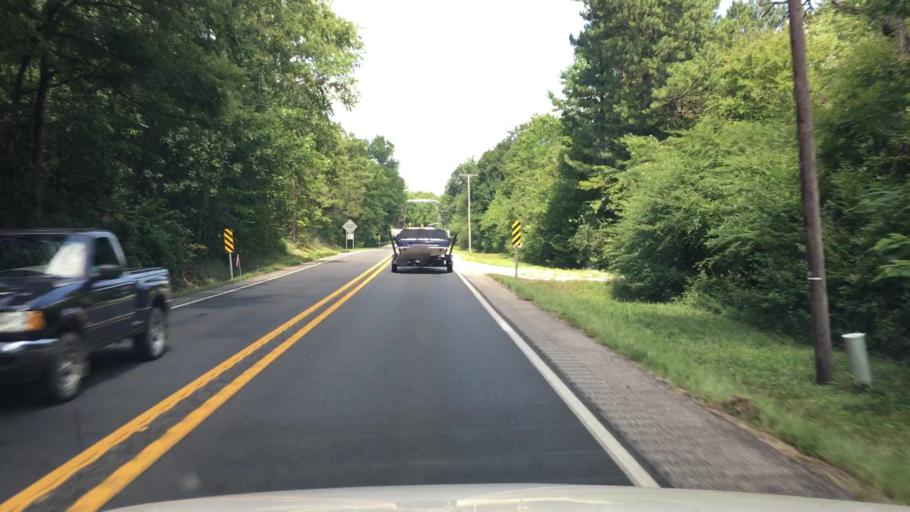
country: US
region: Arkansas
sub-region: Garland County
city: Lake Hamilton
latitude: 34.3855
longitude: -93.1258
